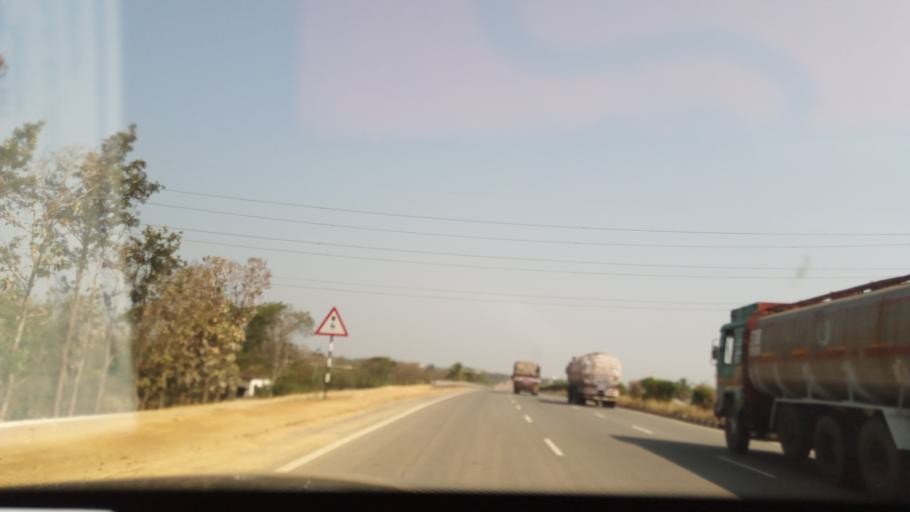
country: IN
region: Karnataka
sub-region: Dharwad
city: Kundgol
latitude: 15.2339
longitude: 75.1410
